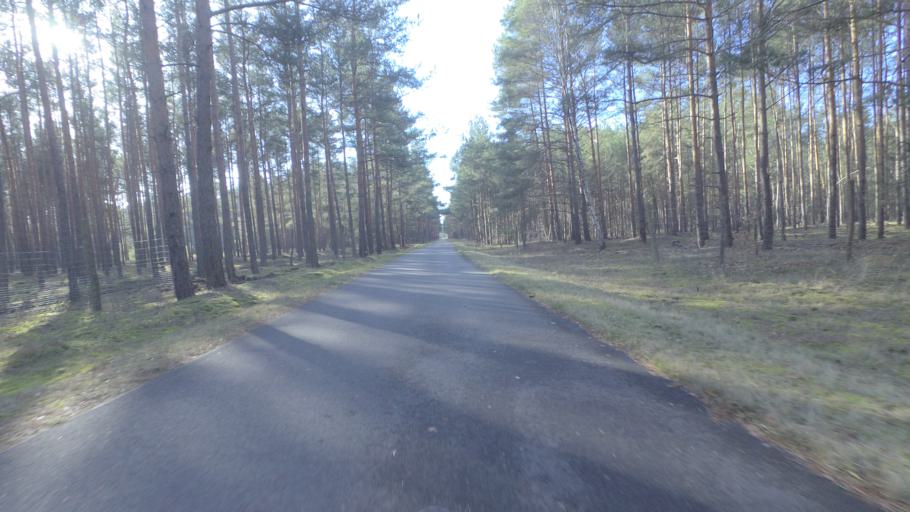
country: DE
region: Brandenburg
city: Luckenwalde
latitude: 52.0516
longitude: 13.1499
